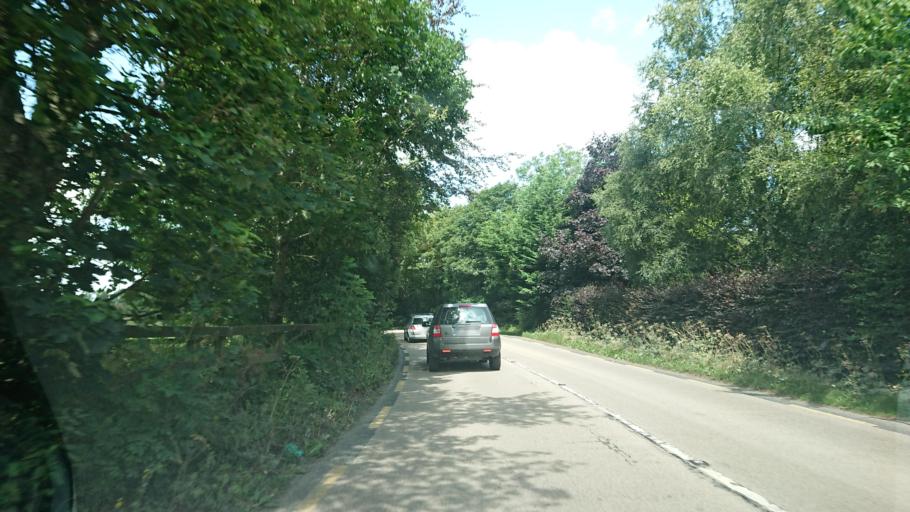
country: IE
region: Leinster
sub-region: Kildare
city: Sallins
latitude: 53.2692
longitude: -6.6709
